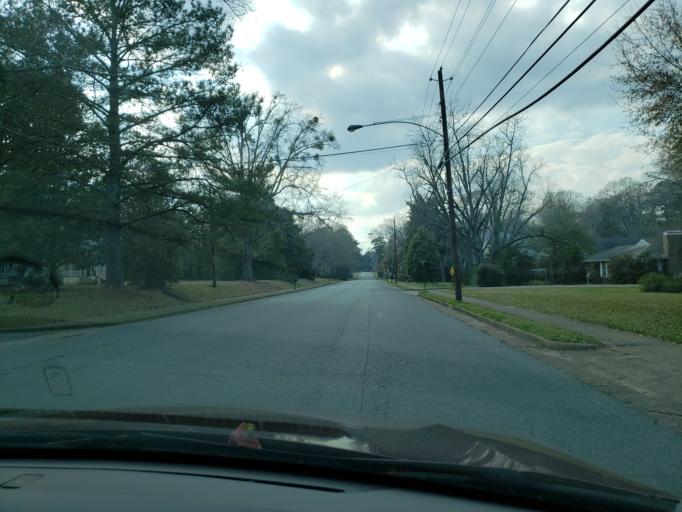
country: US
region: Alabama
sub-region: Hale County
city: Greensboro
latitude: 32.7042
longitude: -87.6007
